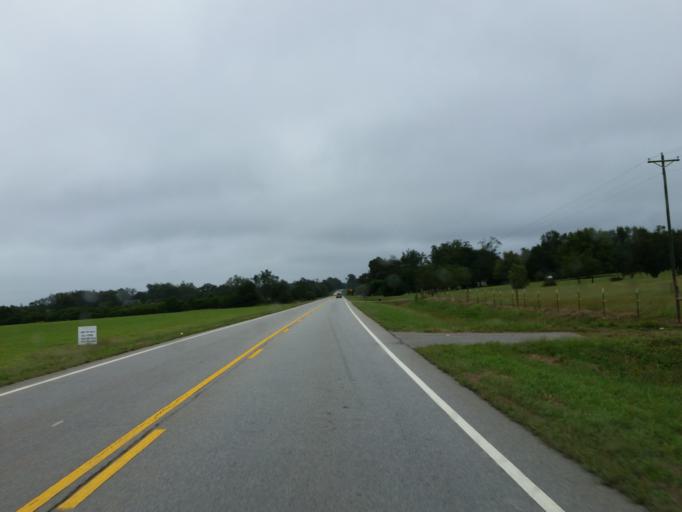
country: US
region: Georgia
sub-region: Lamar County
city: Barnesville
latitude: 32.9795
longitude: -84.1160
